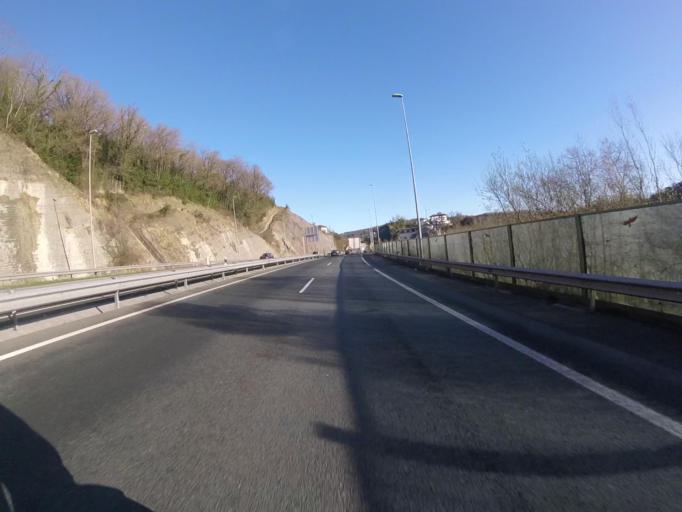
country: ES
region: Basque Country
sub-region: Provincia de Guipuzcoa
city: Astigarraga
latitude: 43.2951
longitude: -1.9581
